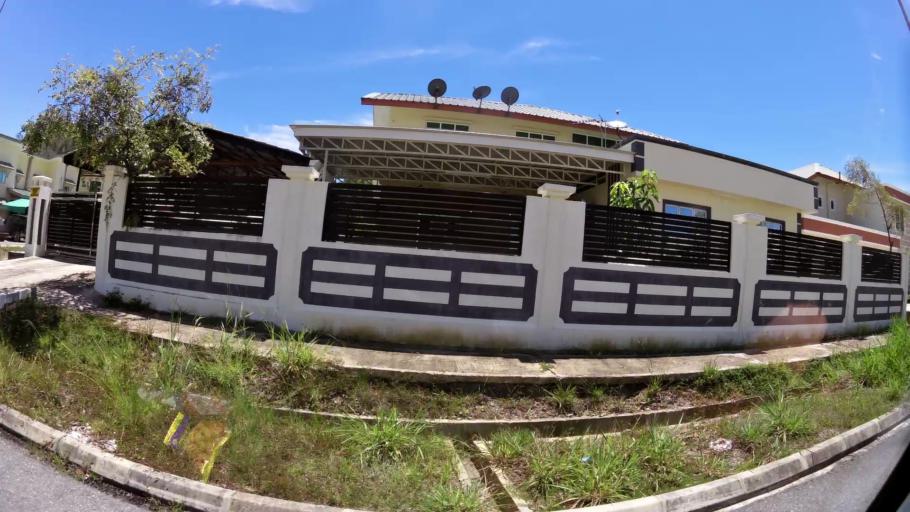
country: BN
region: Brunei and Muara
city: Bandar Seri Begawan
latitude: 5.0325
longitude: 115.0388
